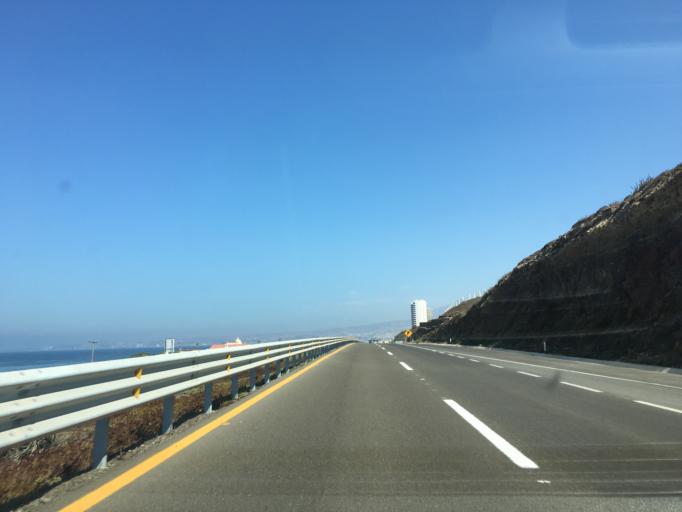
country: MX
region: Baja California
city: Primo Tapia
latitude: 32.1833
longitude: -116.9087
